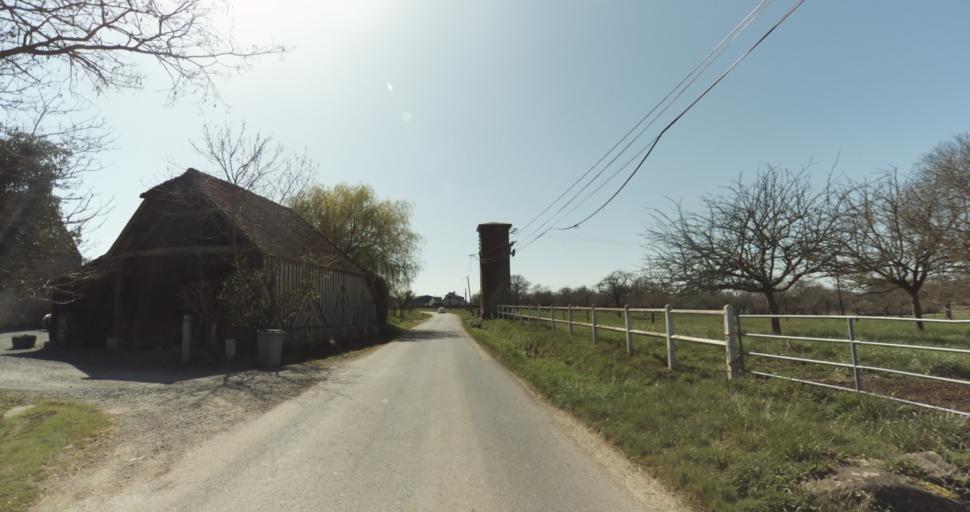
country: FR
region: Lower Normandy
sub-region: Departement du Calvados
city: Saint-Pierre-sur-Dives
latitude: 49.0156
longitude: -0.0059
